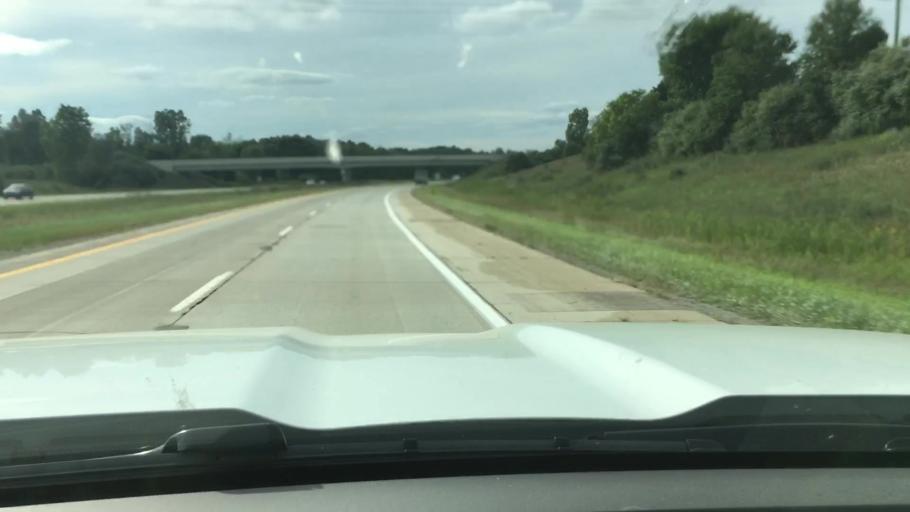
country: US
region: Michigan
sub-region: Lapeer County
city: Lapeer
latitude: 43.0130
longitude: -83.2793
